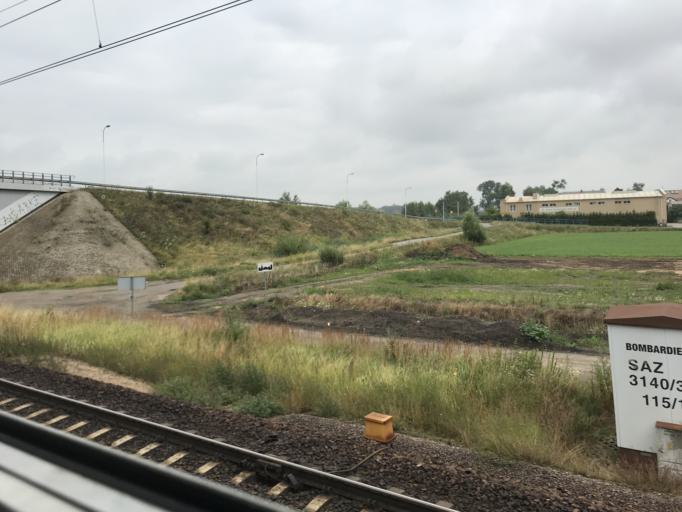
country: PL
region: Pomeranian Voivodeship
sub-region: Powiat gdanski
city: Legowo
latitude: 54.2309
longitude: 18.6477
